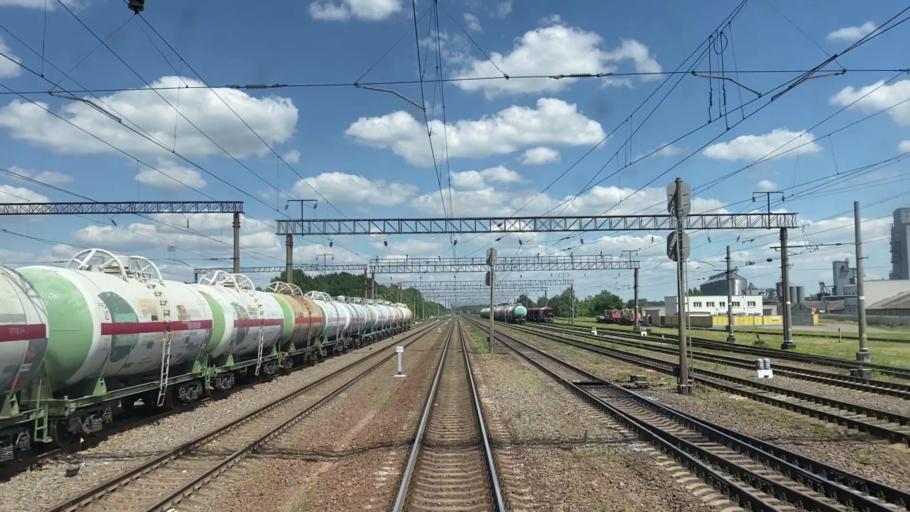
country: BY
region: Brest
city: Zhabinka
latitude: 52.2044
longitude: 24.0255
